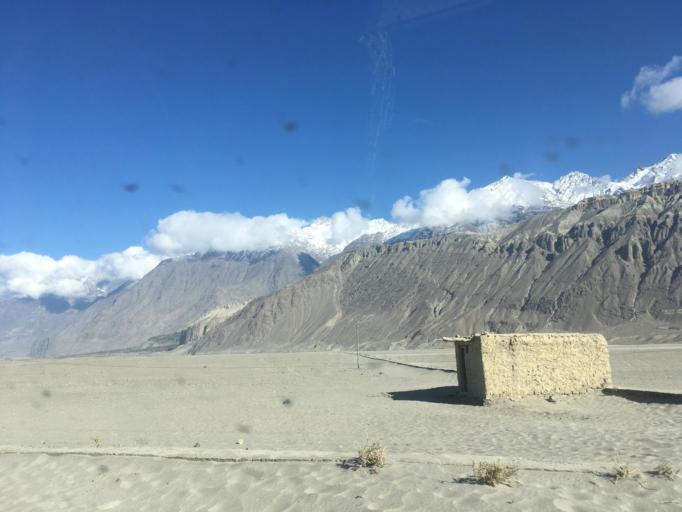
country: PK
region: Gilgit-Baltistan
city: Skardu
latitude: 35.3579
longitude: 75.5404
